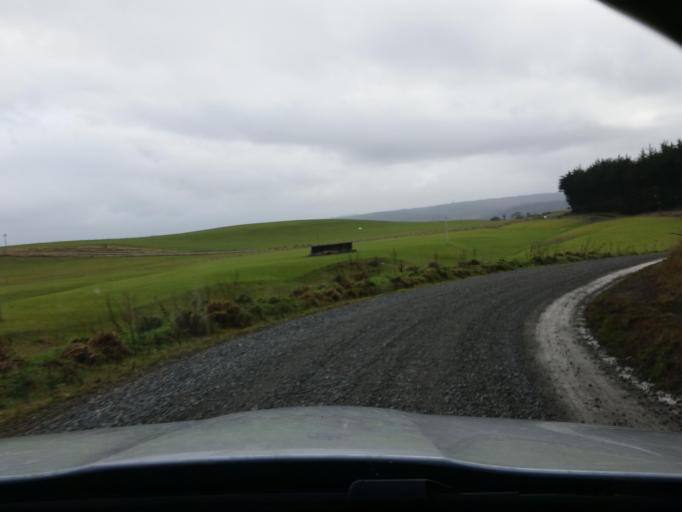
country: NZ
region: Southland
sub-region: Southland District
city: Riverton
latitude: -46.0676
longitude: 167.7645
